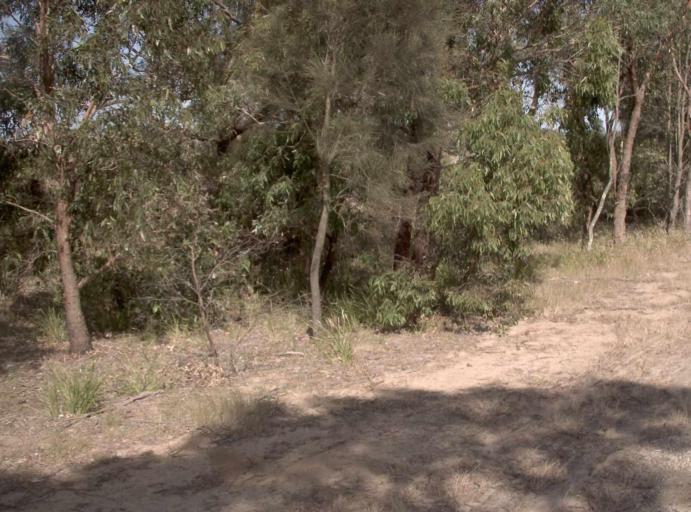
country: AU
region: Victoria
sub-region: Wellington
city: Sale
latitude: -38.3416
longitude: 147.1672
